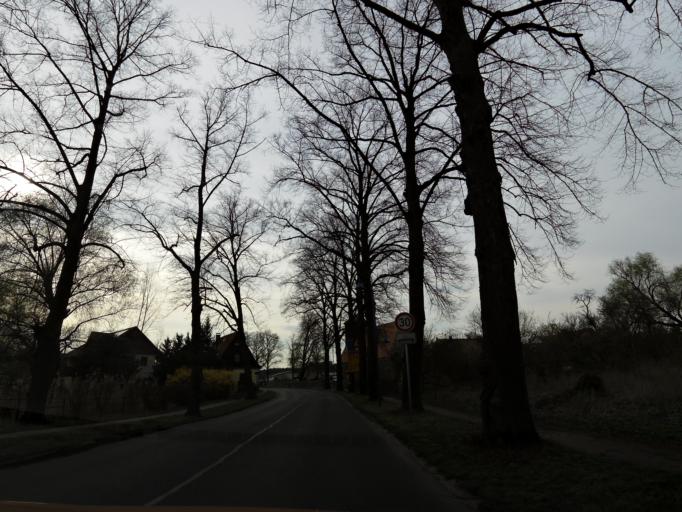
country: DE
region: Brandenburg
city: Bestensee
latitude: 52.2432
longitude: 13.6289
